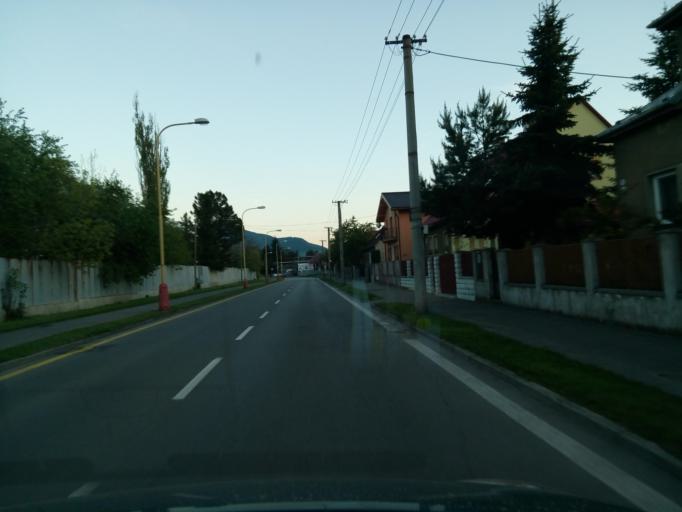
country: SK
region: Zilinsky
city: Ruzomberok
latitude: 49.0747
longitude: 19.3094
